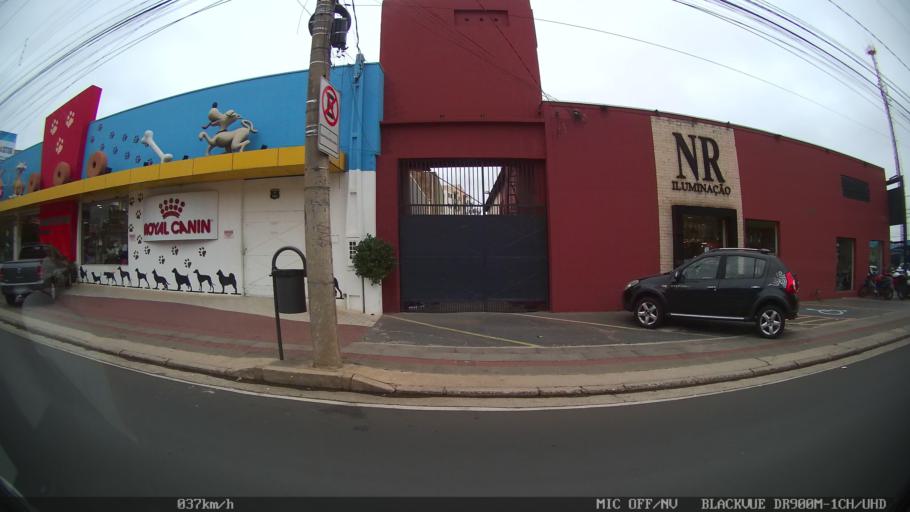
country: BR
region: Sao Paulo
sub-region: Sao Jose Do Rio Preto
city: Sao Jose do Rio Preto
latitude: -20.8214
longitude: -49.3929
